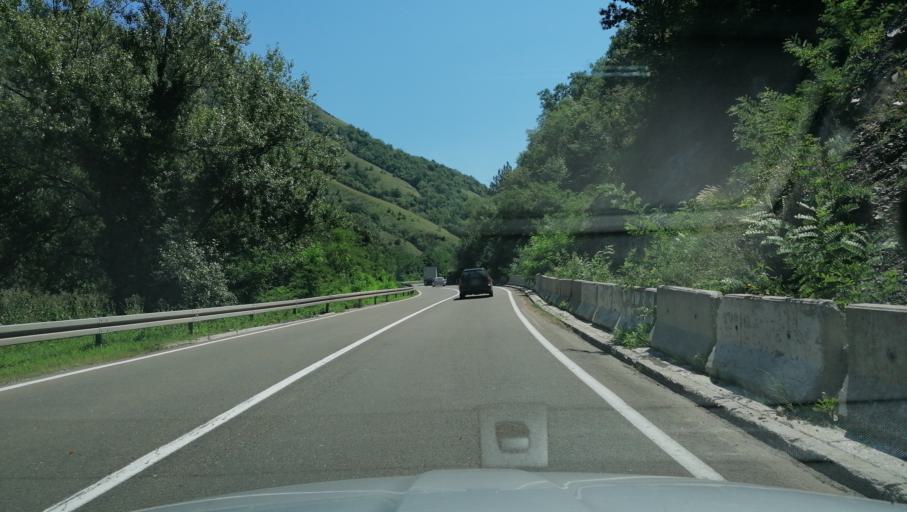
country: RS
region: Central Serbia
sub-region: Raski Okrug
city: Kraljevo
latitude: 43.5814
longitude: 20.5842
